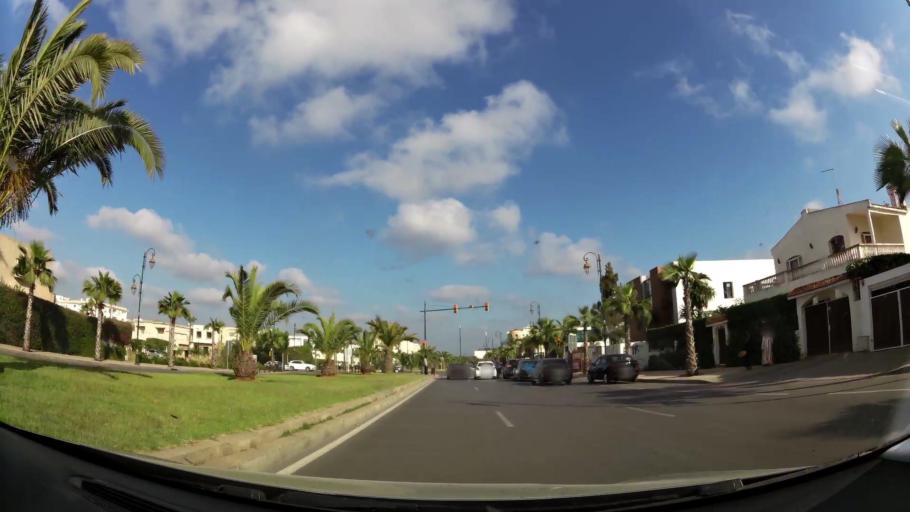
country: MA
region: Rabat-Sale-Zemmour-Zaer
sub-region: Skhirate-Temara
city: Temara
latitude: 33.9523
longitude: -6.8627
